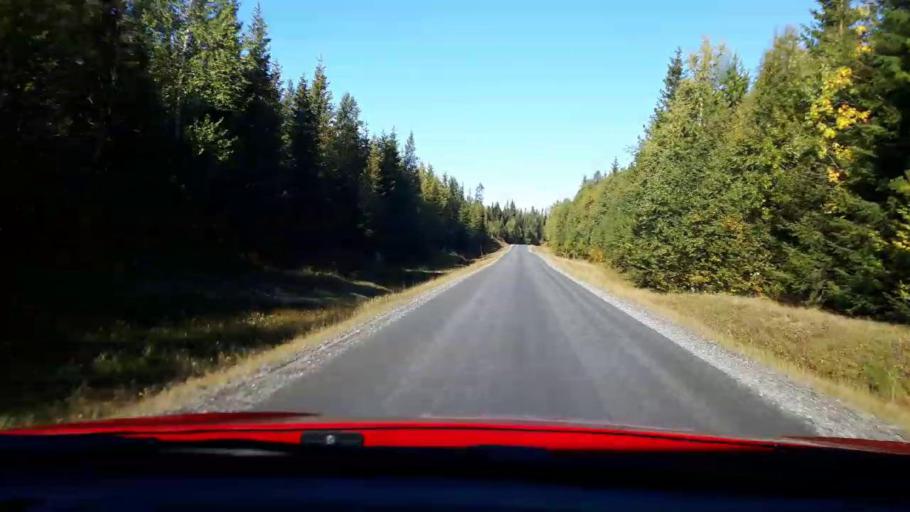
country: NO
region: Nord-Trondelag
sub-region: Lierne
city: Sandvika
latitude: 64.5291
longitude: 14.0471
